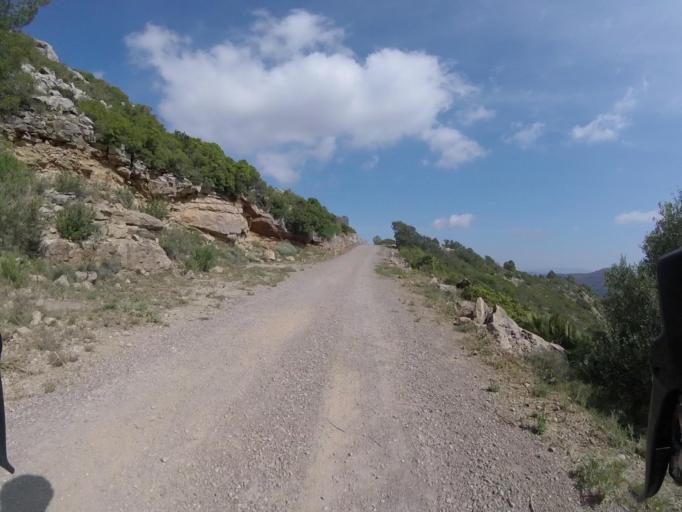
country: ES
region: Valencia
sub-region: Provincia de Castello
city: Benicassim
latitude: 40.0993
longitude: 0.0451
